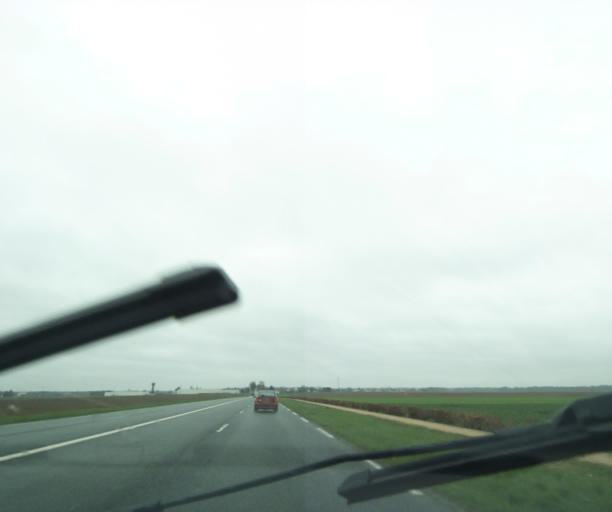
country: FR
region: Centre
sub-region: Departement du Loiret
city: Chevilly
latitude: 48.0434
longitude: 1.8742
